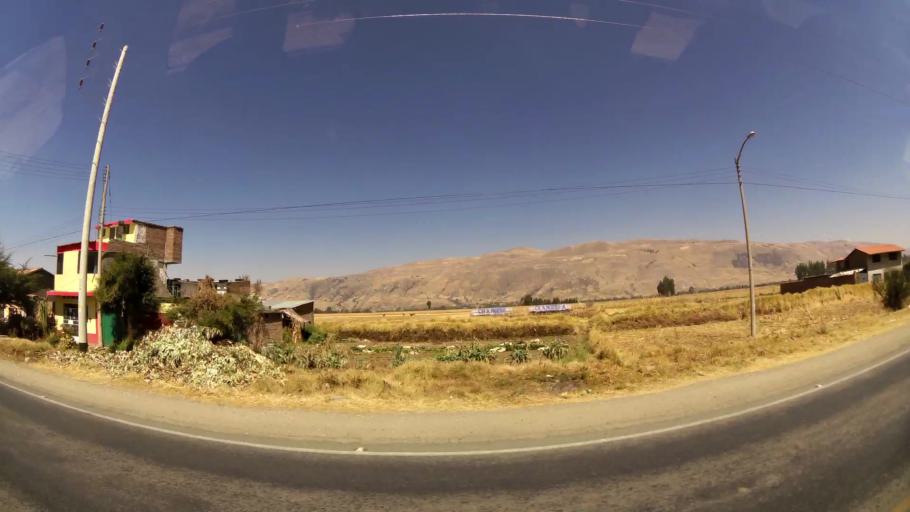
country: PE
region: Junin
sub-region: Provincia de Jauja
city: San Lorenzo
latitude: -11.8312
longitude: -75.4005
